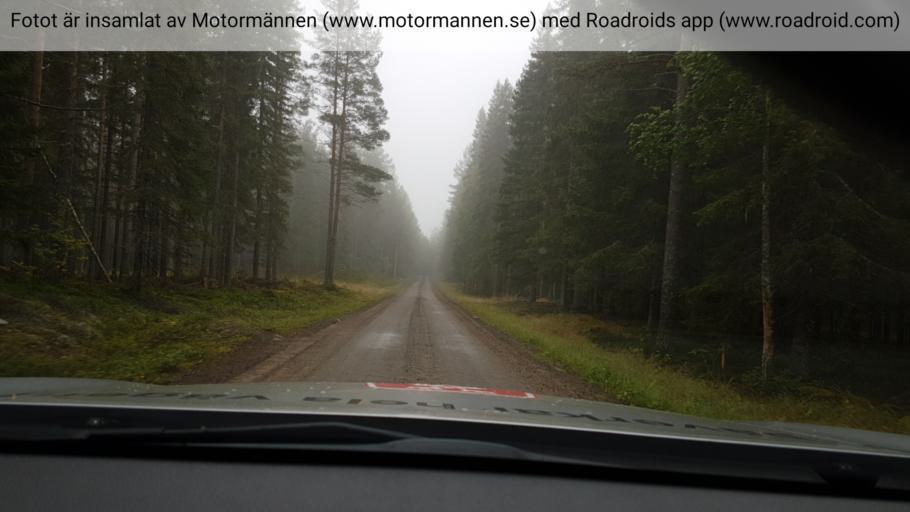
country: SE
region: Vaesterbotten
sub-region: Robertsfors Kommun
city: Robertsfors
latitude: 64.2411
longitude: 20.5655
